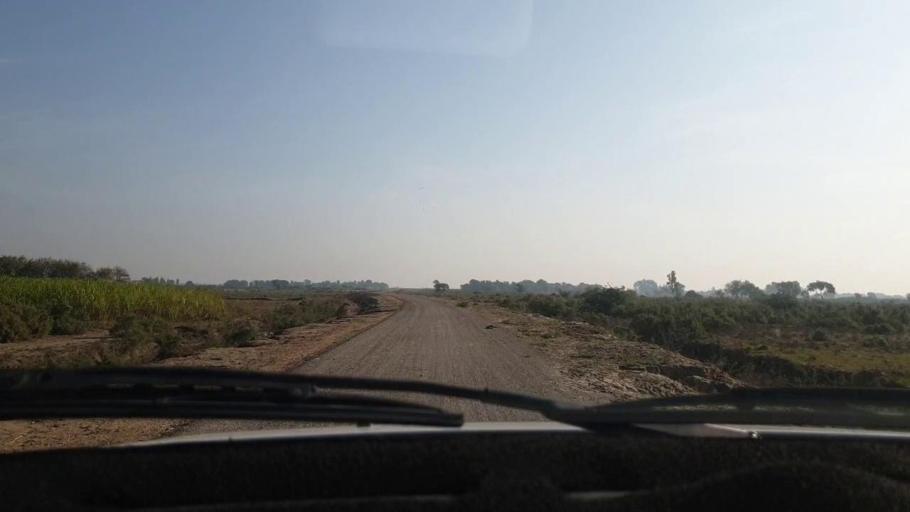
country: PK
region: Sindh
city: Tando Muhammad Khan
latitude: 25.0271
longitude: 68.4759
